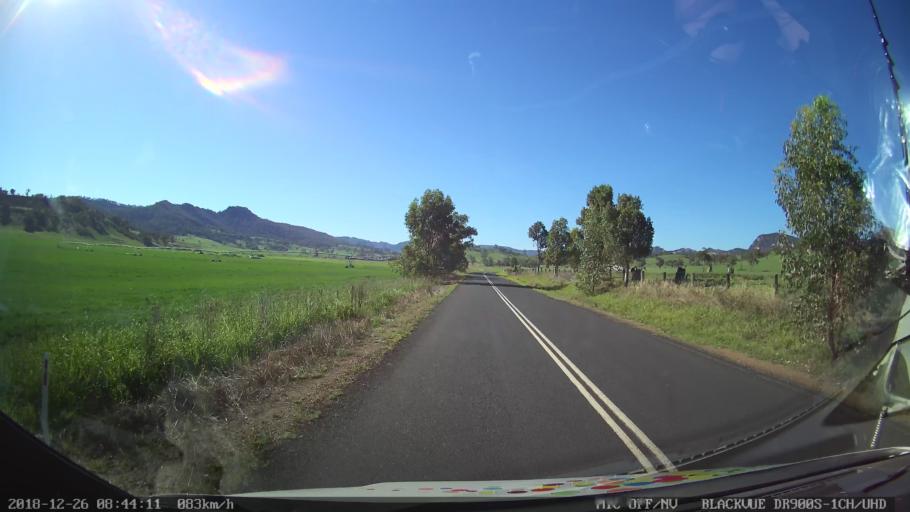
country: AU
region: New South Wales
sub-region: Mid-Western Regional
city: Kandos
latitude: -32.5113
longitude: 150.0806
